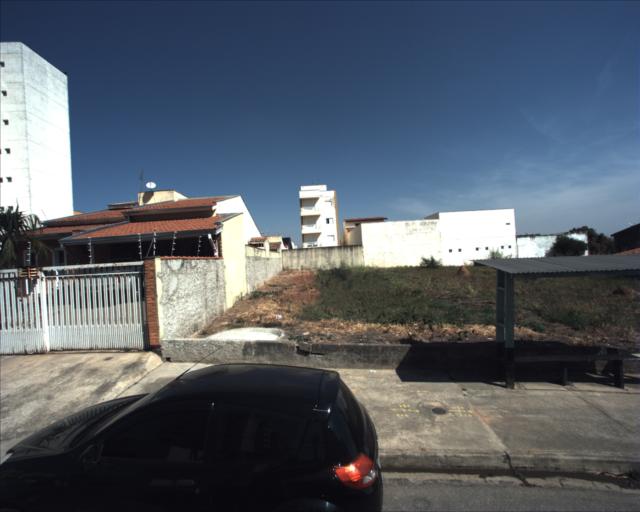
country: BR
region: Sao Paulo
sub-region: Sorocaba
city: Sorocaba
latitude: -23.4663
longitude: -47.4334
